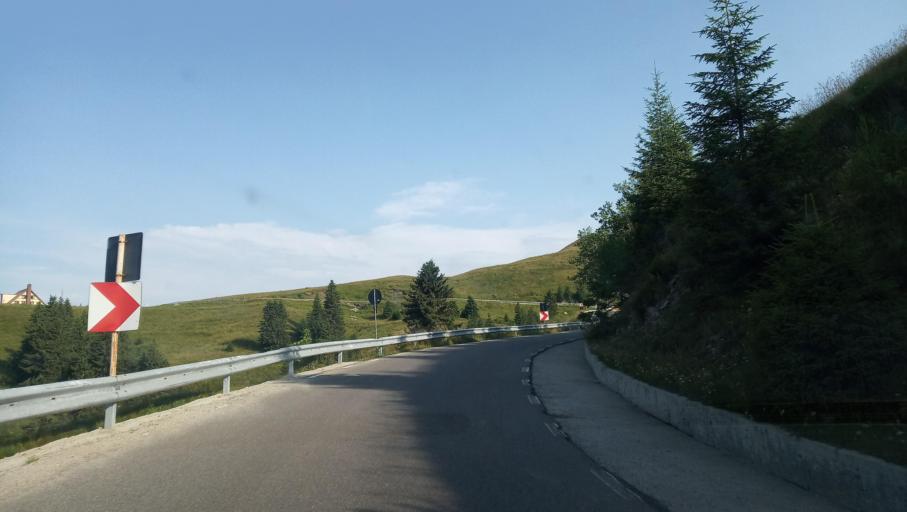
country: RO
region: Dambovita
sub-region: Comuna Moroeni
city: Glod
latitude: 45.3256
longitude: 25.4673
